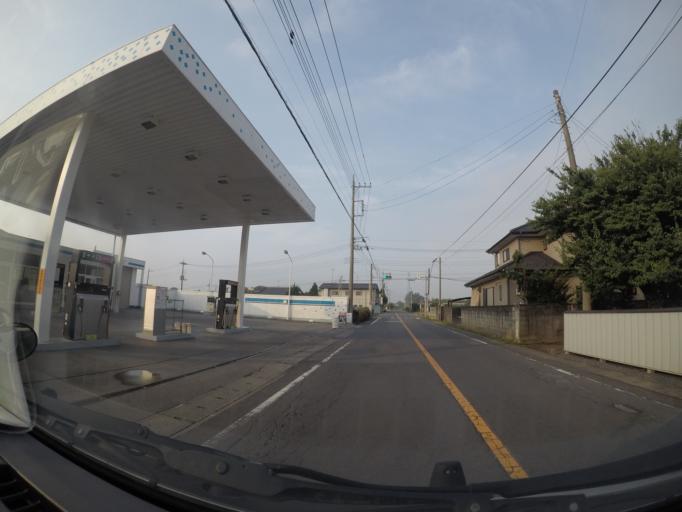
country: JP
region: Tochigi
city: Fujioka
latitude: 36.2700
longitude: 139.6763
